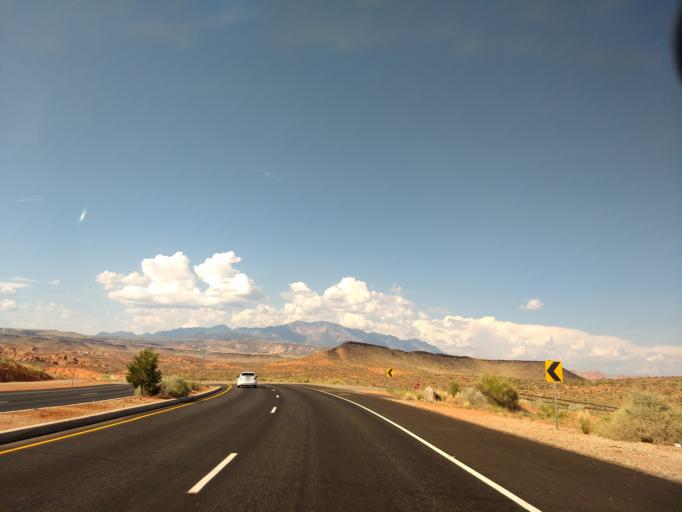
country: US
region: Utah
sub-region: Washington County
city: Saint George
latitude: 37.1257
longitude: -113.5830
